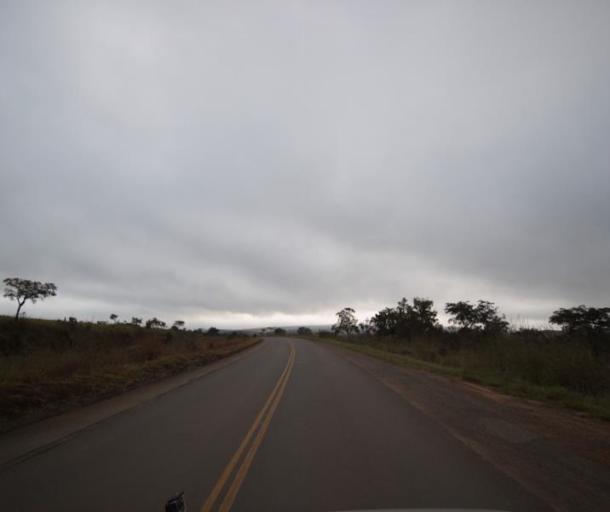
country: BR
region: Goias
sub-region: Pirenopolis
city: Pirenopolis
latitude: -15.8688
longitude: -48.7755
